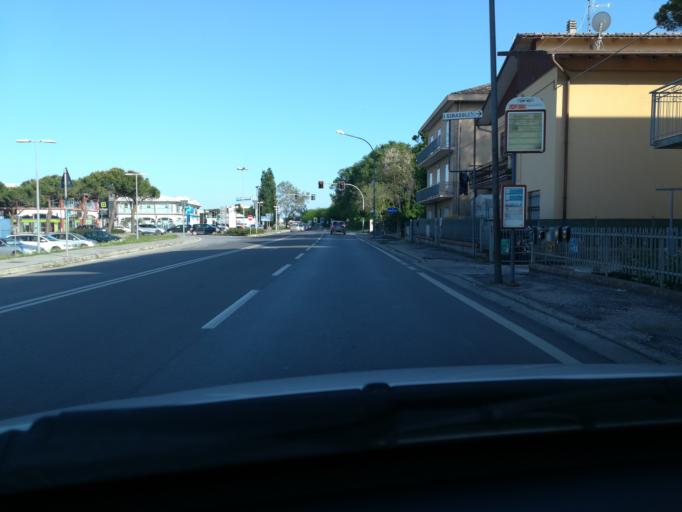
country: IT
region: Emilia-Romagna
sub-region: Provincia di Rimini
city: Misano Adriatico
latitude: 43.9794
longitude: 12.6856
